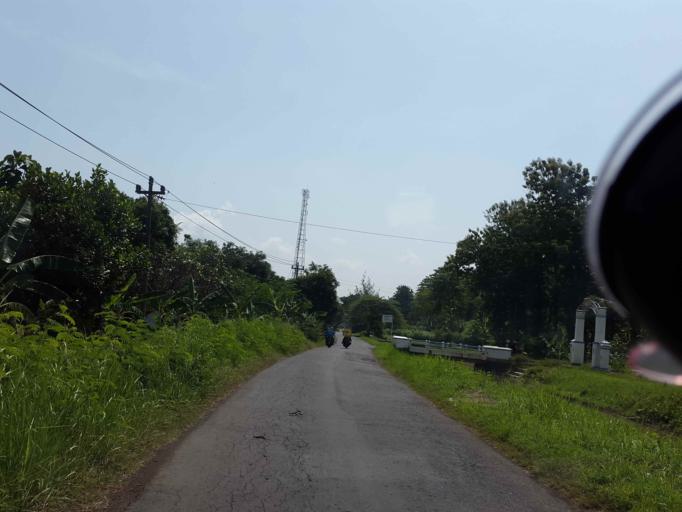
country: ID
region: Central Java
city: Pemalang
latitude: -6.9439
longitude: 109.3858
